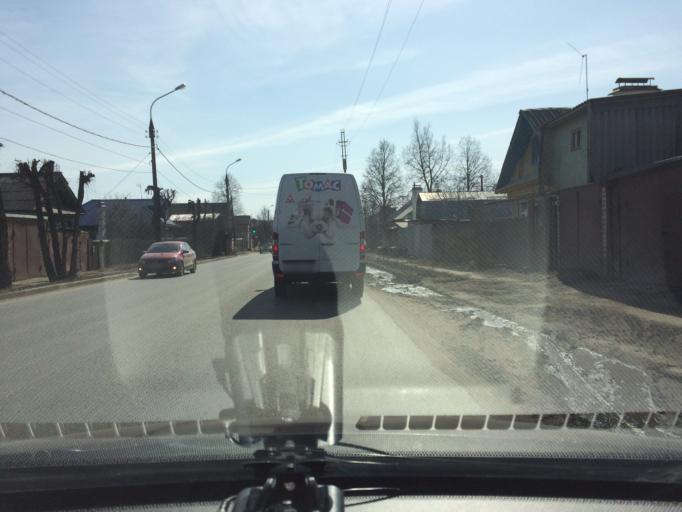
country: RU
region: Mariy-El
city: Yoshkar-Ola
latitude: 56.6471
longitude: 47.9056
